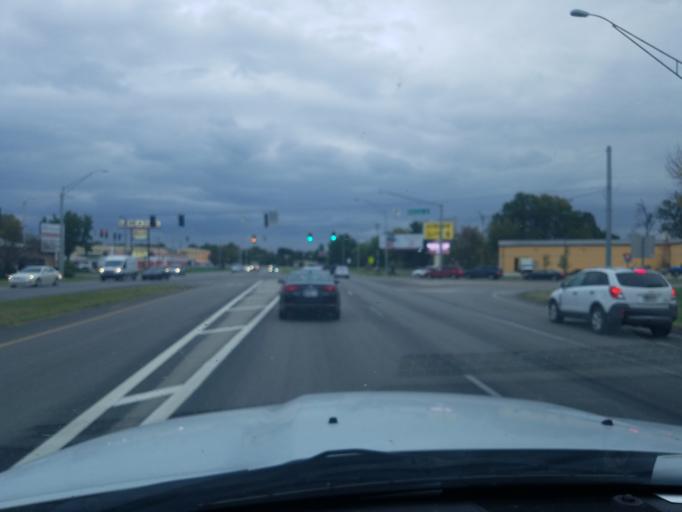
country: US
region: Indiana
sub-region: Vanderburgh County
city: Evansville
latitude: 37.9505
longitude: -87.5427
